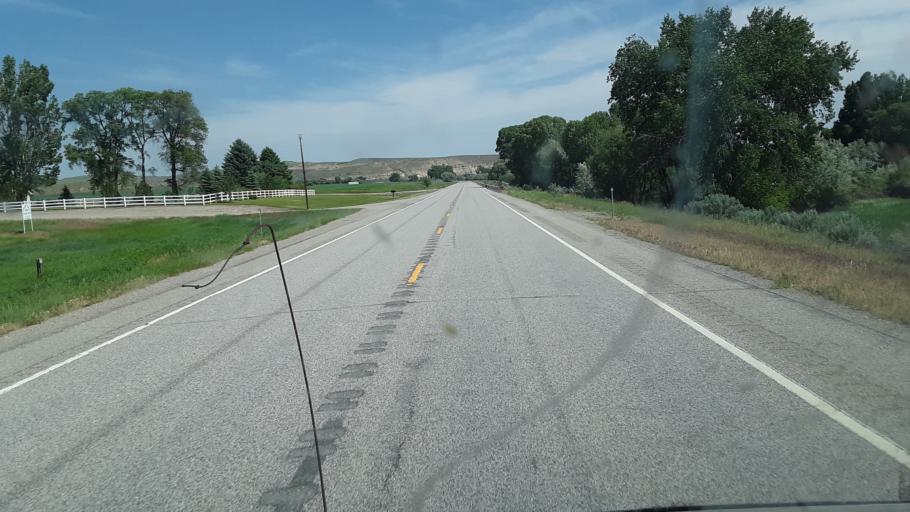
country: US
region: Montana
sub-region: Carbon County
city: Red Lodge
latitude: 45.0864
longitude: -109.0290
